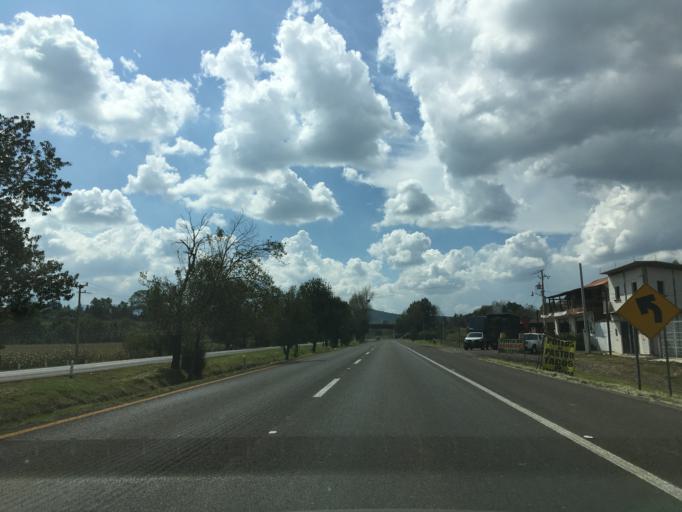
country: MX
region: Michoacan
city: Huiramba
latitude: 19.5457
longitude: -101.4470
